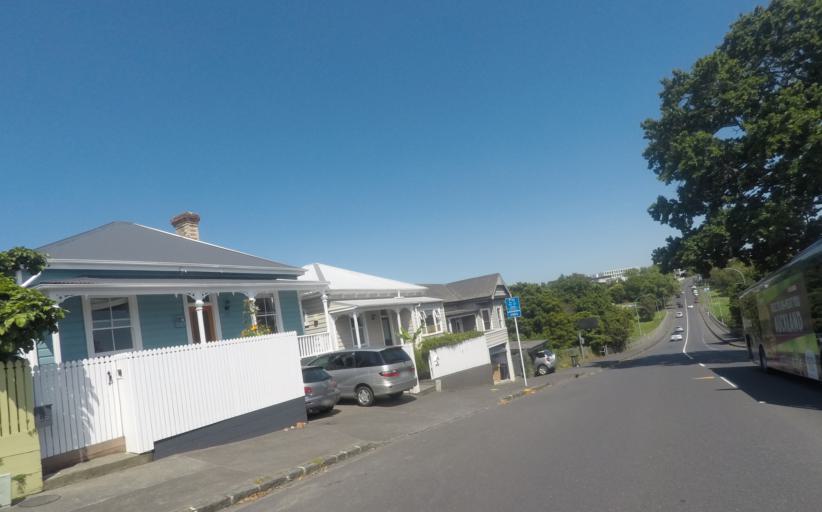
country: NZ
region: Auckland
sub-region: Auckland
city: Auckland
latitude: -36.8674
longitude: 174.7456
